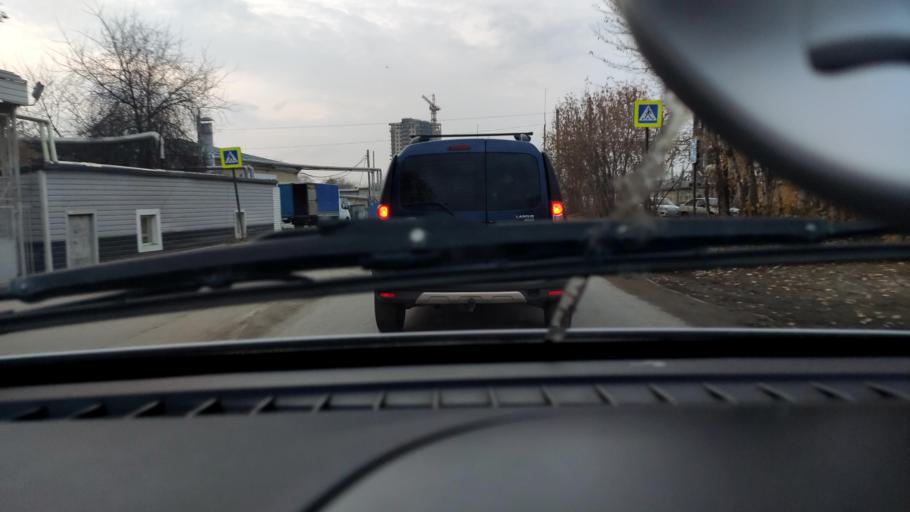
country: RU
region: Perm
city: Perm
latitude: 57.9720
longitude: 56.1884
